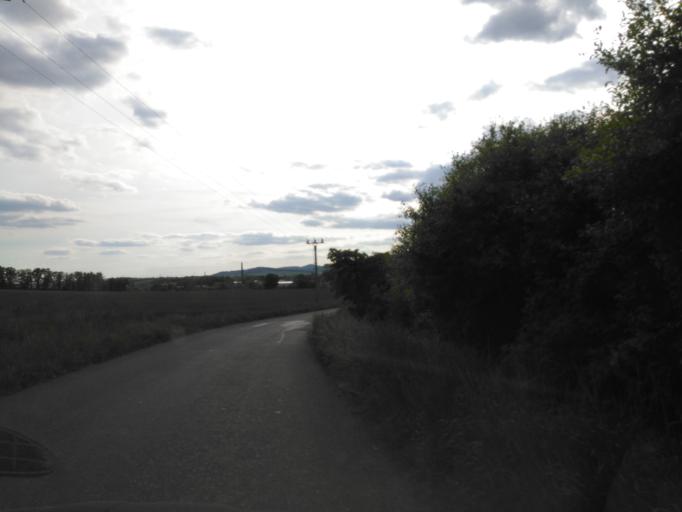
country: CZ
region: Central Bohemia
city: Zdice
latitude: 49.9124
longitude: 13.9979
